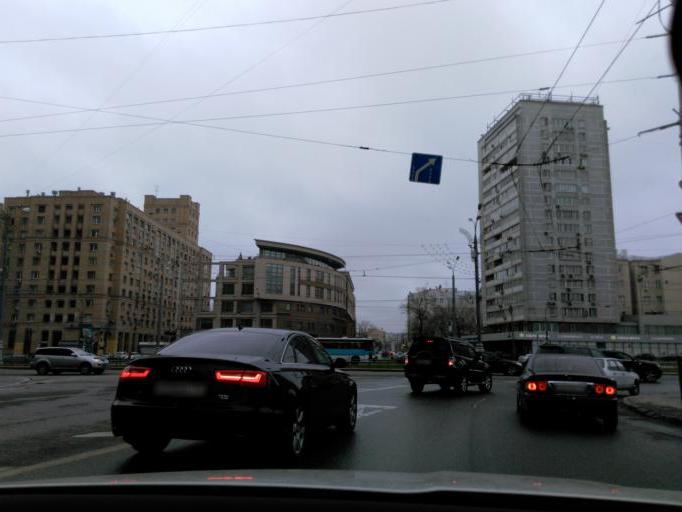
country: RU
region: Moscow
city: Moscow
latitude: 55.7731
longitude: 37.6042
